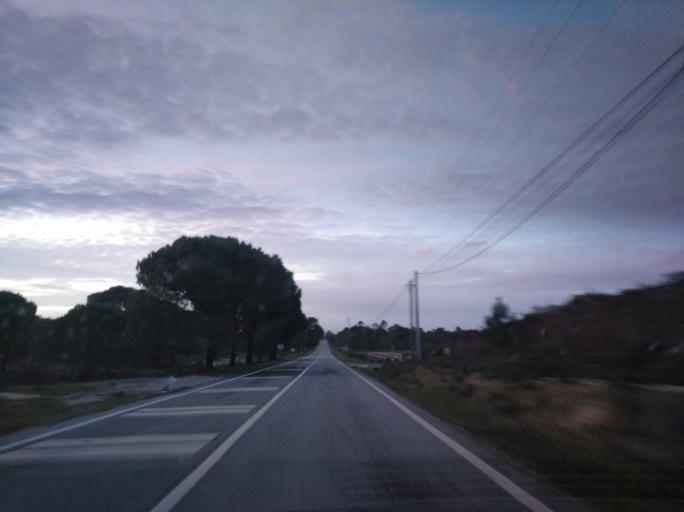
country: PT
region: Setubal
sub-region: Grandola
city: Grandola
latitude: 38.2711
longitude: -8.6903
